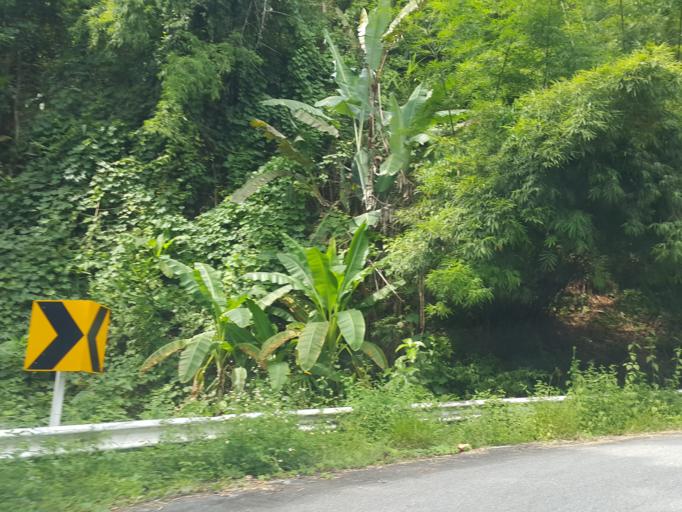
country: TH
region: Mae Hong Son
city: Mae Hong Son
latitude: 19.4832
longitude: 97.9612
